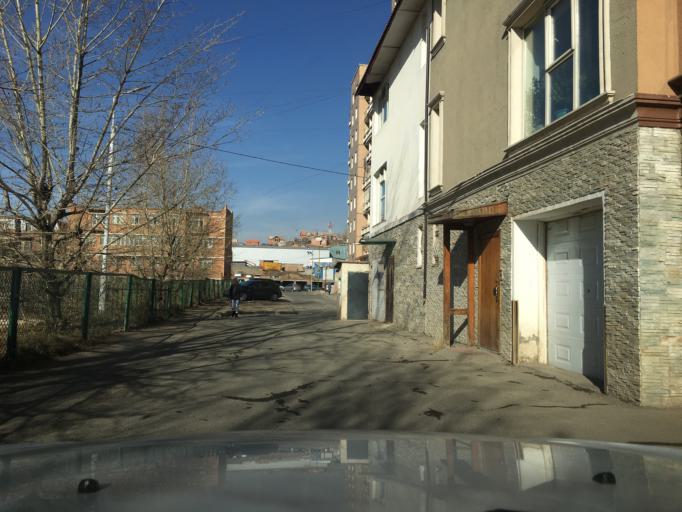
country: MN
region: Ulaanbaatar
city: Ulaanbaatar
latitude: 47.9158
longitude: 106.8509
